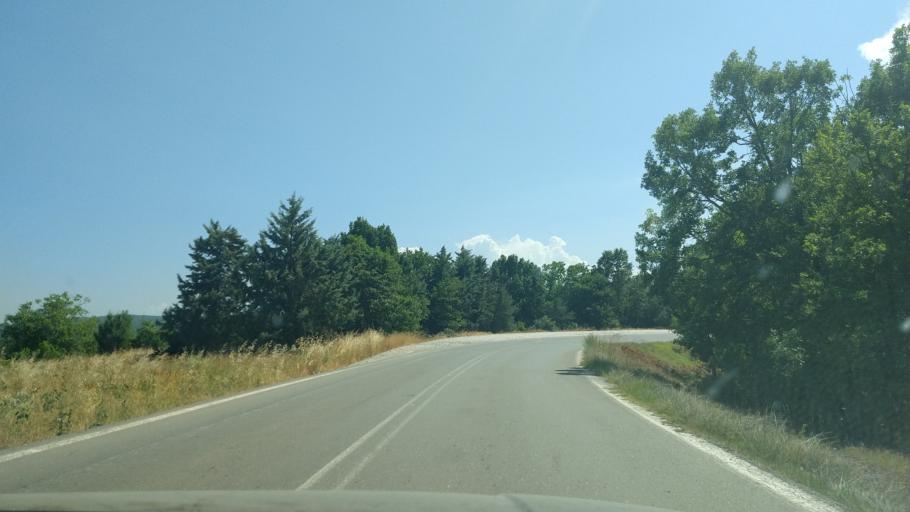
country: GR
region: West Macedonia
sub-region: Nomos Grevenon
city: Grevena
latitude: 40.0670
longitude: 21.4569
